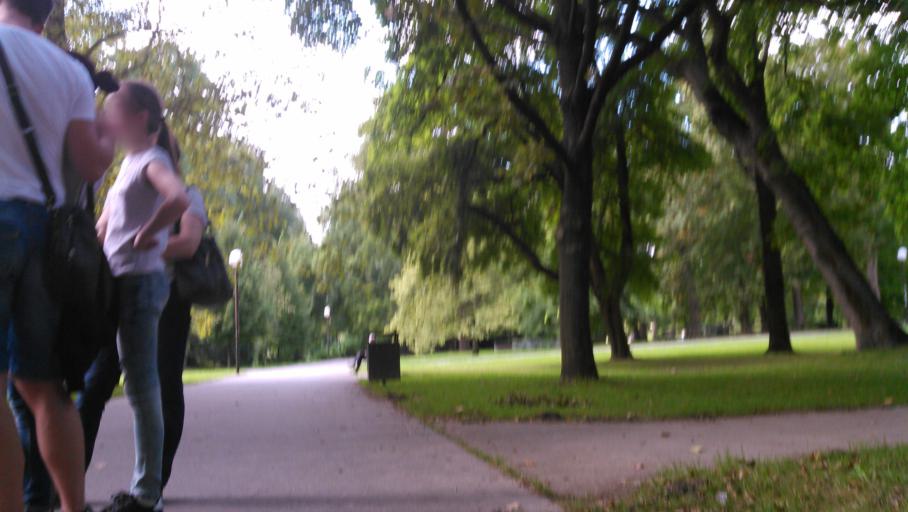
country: SK
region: Bratislavsky
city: Bratislava
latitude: 48.1339
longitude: 17.1120
